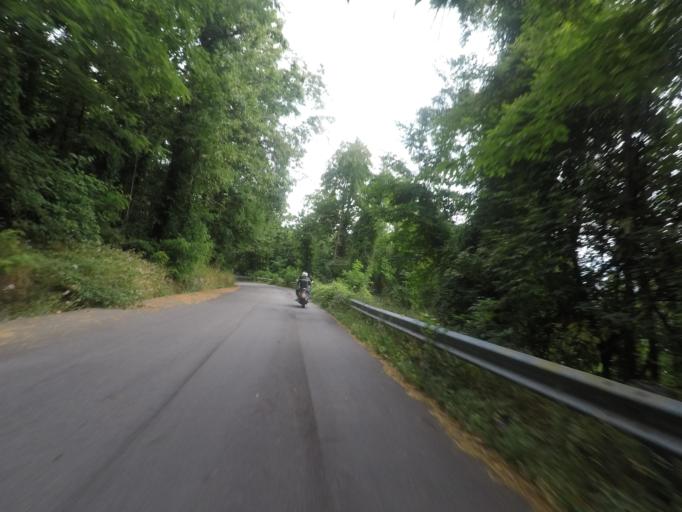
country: IT
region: Tuscany
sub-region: Provincia di Lucca
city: Careggine
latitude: 44.1129
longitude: 10.3605
